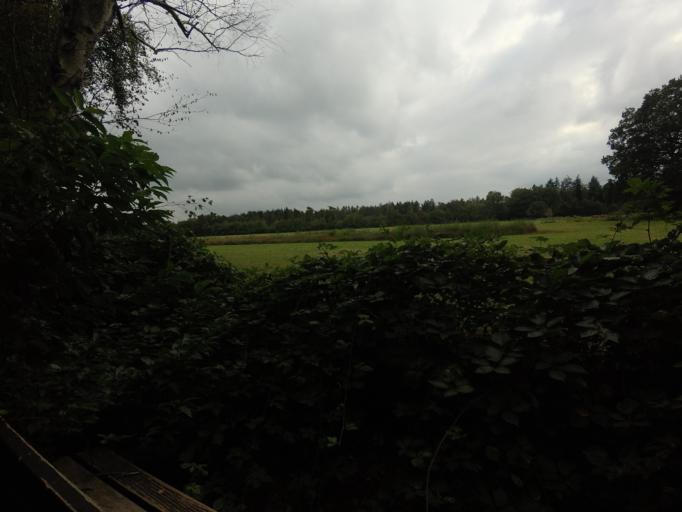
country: NL
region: Gelderland
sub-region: Gemeente Lochem
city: Harfsen
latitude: 52.2768
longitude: 6.2801
